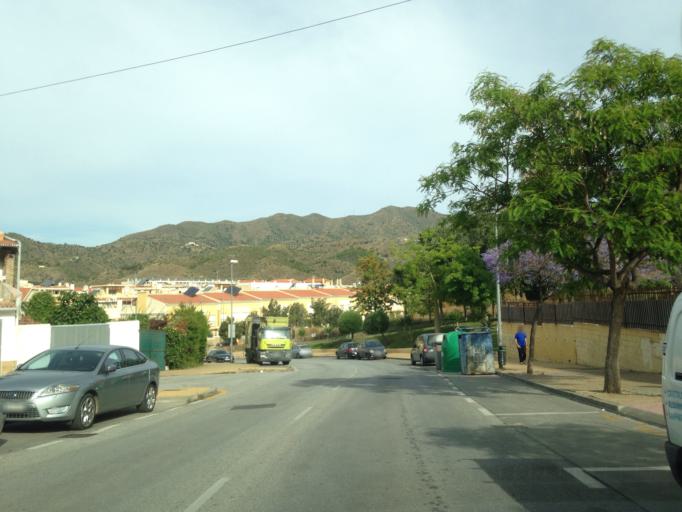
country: ES
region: Andalusia
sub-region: Provincia de Malaga
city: Malaga
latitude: 36.7528
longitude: -4.4219
